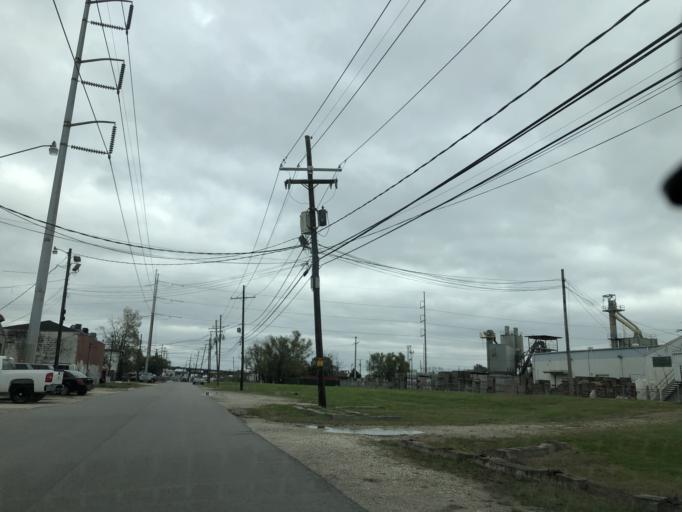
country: US
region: Louisiana
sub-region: Jefferson Parish
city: Metairie Terrace
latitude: 29.9745
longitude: -90.1636
